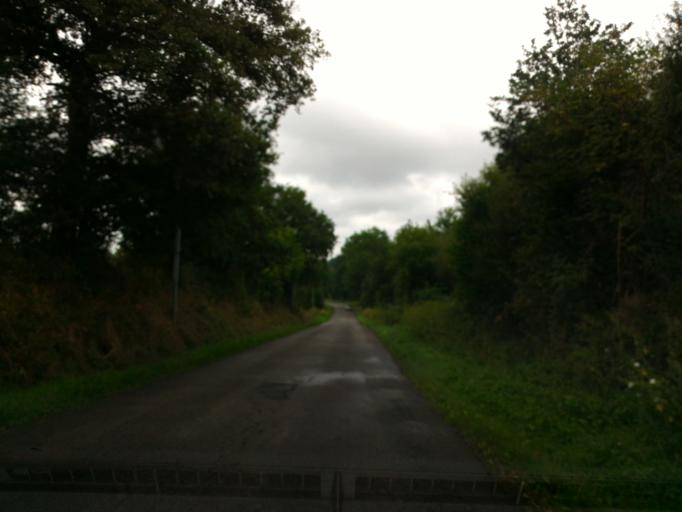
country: FR
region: Poitou-Charentes
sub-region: Departement de la Charente
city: Etagnac
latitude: 45.9427
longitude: 0.7866
